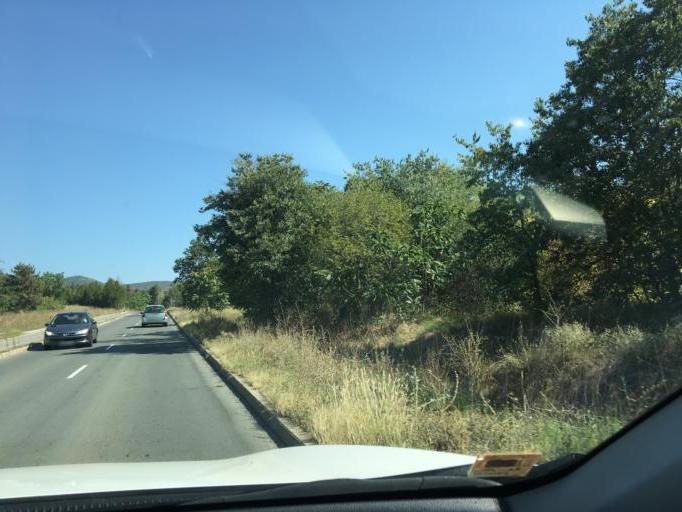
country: BG
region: Burgas
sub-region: Obshtina Kameno
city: Kameno
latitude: 42.6156
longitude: 27.3935
